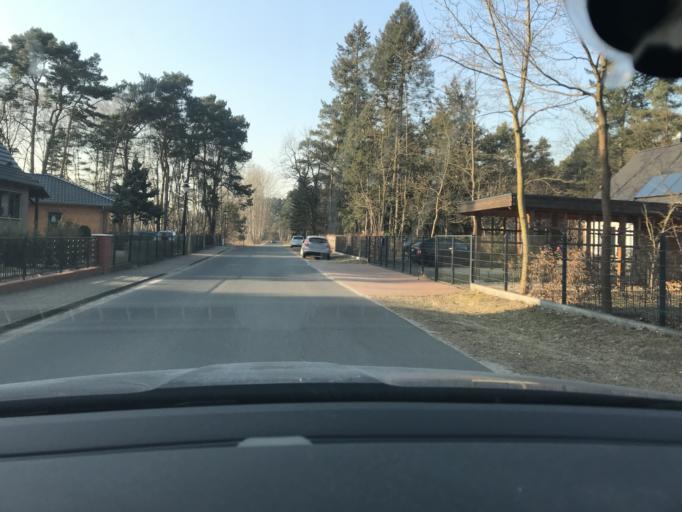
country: DE
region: Brandenburg
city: Munchehofe
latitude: 52.2159
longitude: 13.7815
